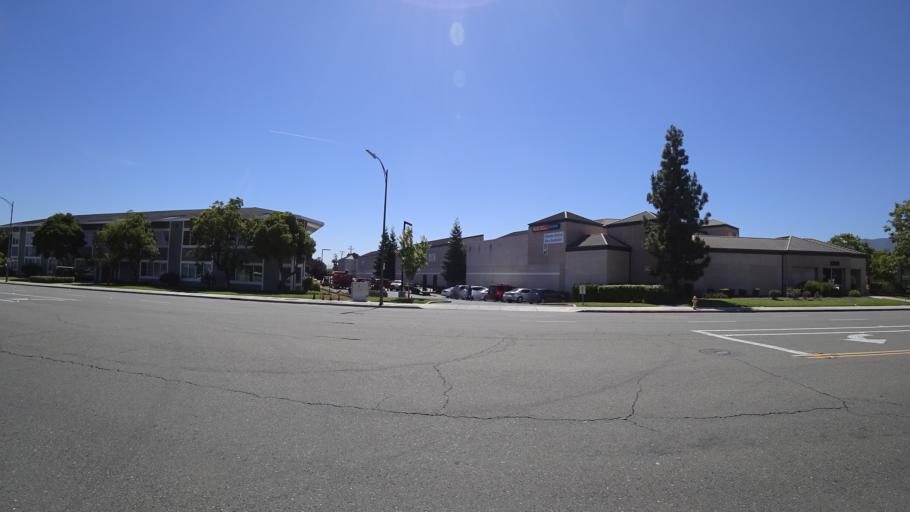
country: US
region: California
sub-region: Santa Clara County
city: Cambrian Park
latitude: 37.2652
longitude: -121.9421
